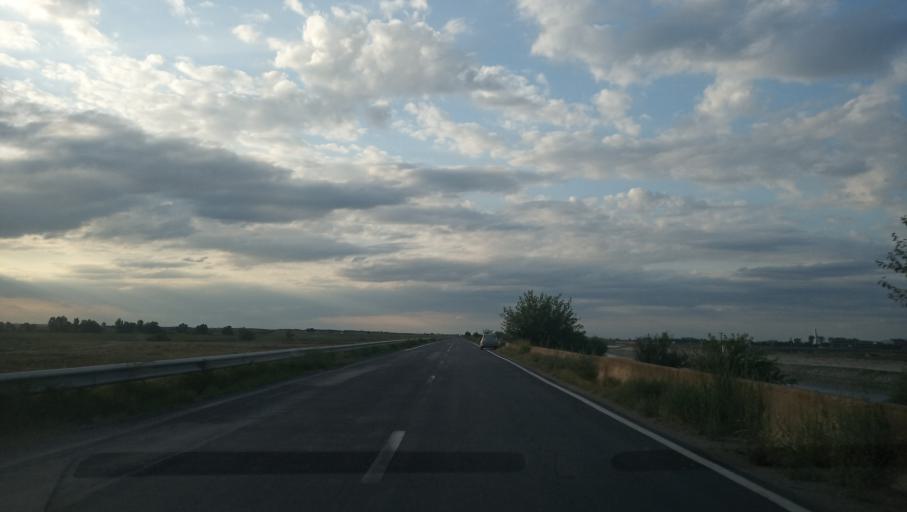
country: RO
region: Calarasi
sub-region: Municipiul Calarasi
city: Calarasi
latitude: 44.1944
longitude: 27.2960
